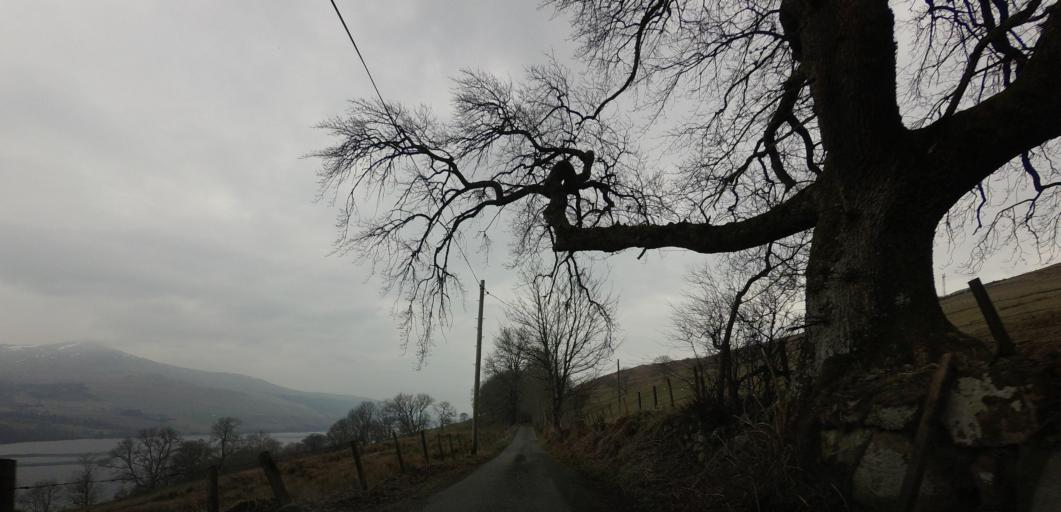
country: GB
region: Scotland
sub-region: Perth and Kinross
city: Comrie
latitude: 56.5100
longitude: -4.1361
